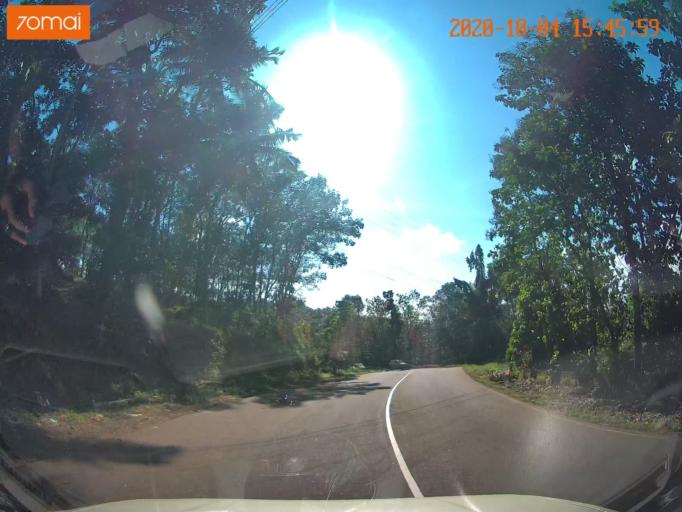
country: IN
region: Kerala
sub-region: Kottayam
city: Palackattumala
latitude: 9.7605
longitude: 76.5766
